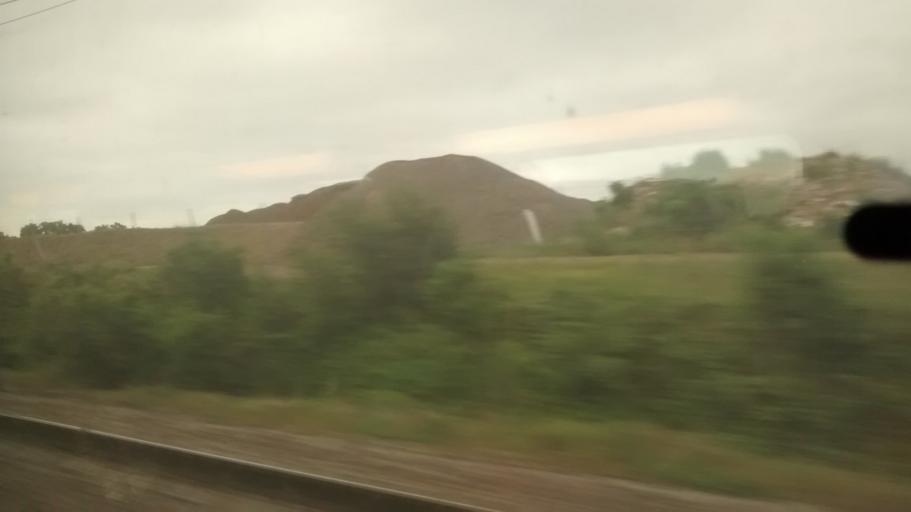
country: FR
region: Bourgogne
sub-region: Departement de l'Yonne
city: Villeneuve-la-Guyard
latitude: 48.3718
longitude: 3.0780
